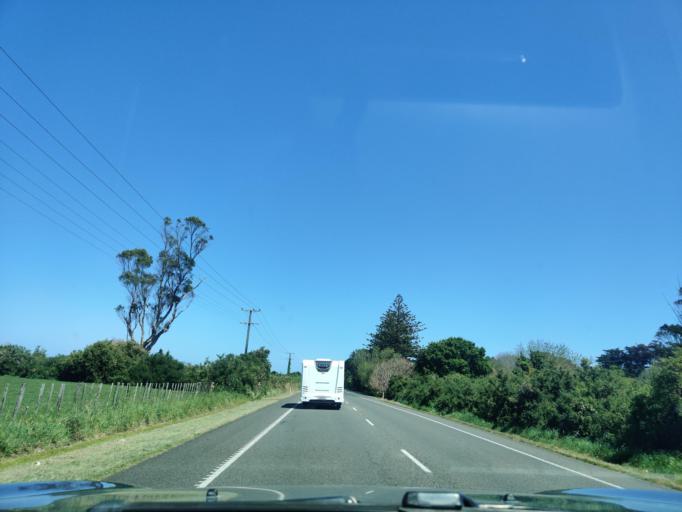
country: NZ
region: Taranaki
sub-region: South Taranaki District
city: Patea
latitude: -39.8081
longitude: 174.7550
